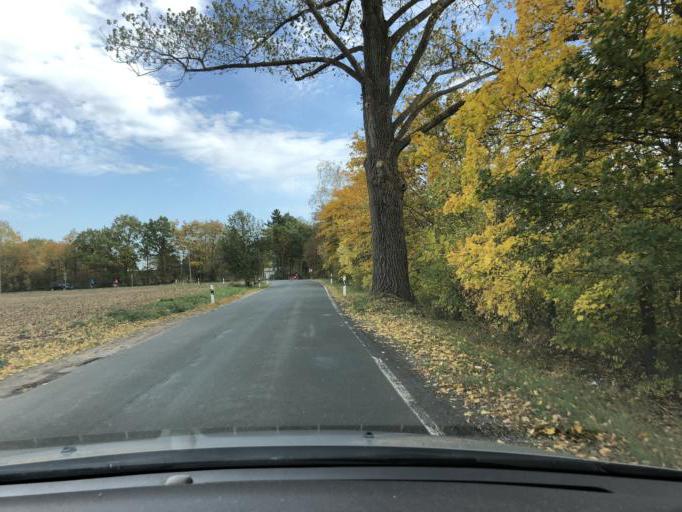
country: DE
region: Thuringia
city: Tonndorf
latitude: 50.8799
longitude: 11.1924
